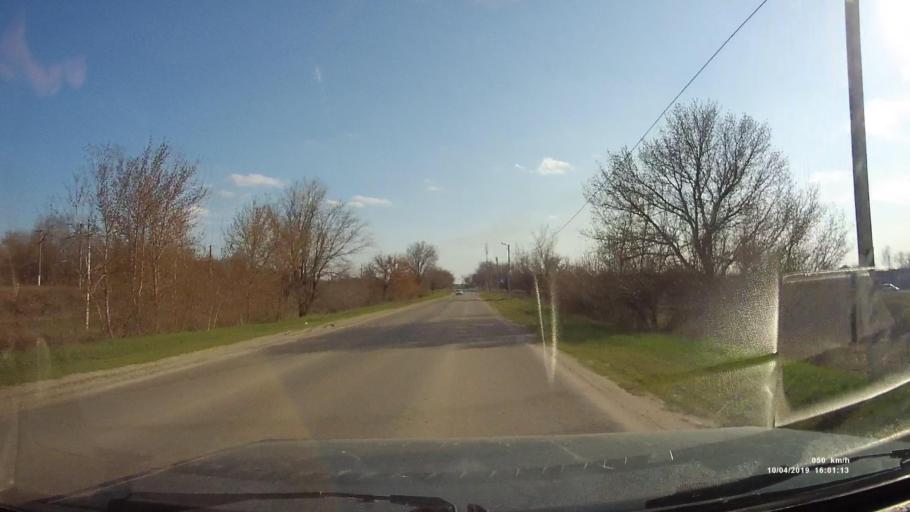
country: RU
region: Rostov
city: Masalovka
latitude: 48.3785
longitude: 40.2618
